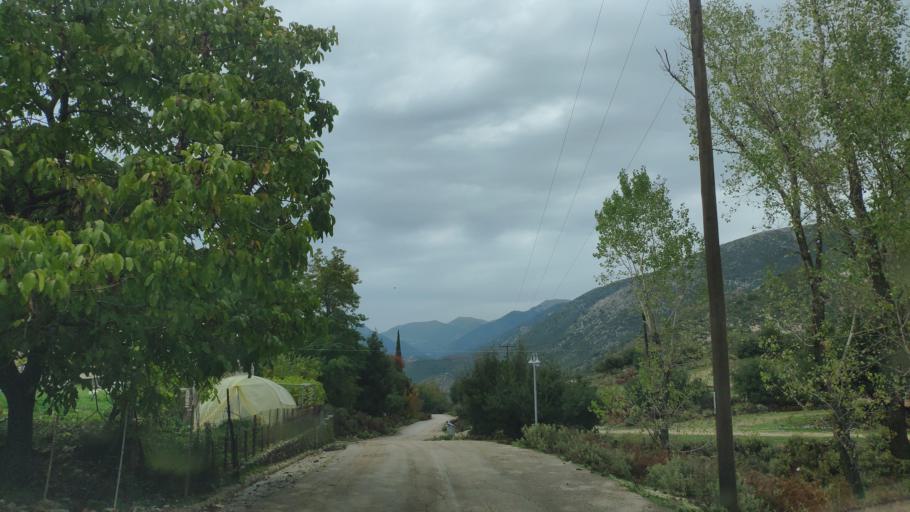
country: GR
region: Epirus
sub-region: Nomos Prevezis
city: Kanalaki
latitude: 39.3610
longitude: 20.6407
